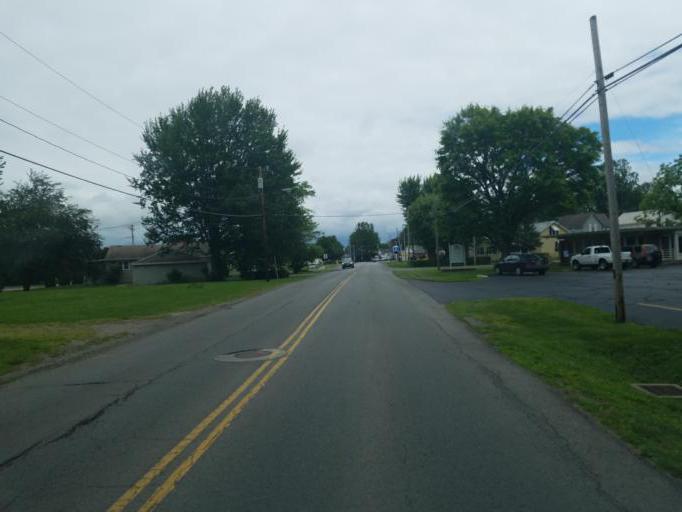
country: US
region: Ohio
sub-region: Crawford County
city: Galion
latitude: 40.7350
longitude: -82.8102
